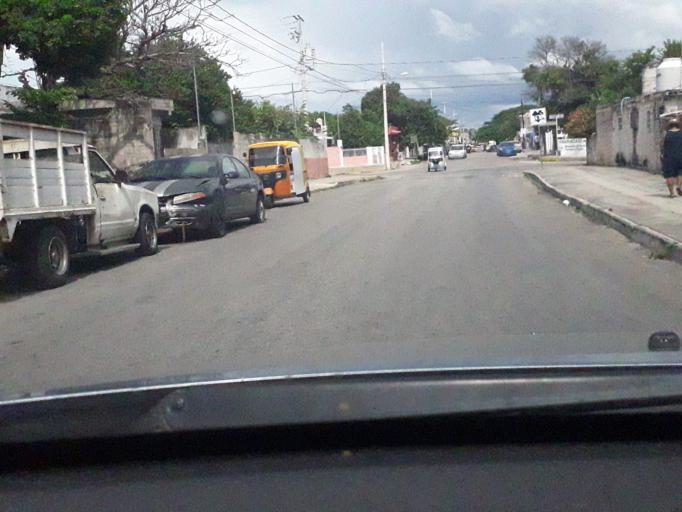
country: MX
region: Yucatan
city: Merida
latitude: 20.9681
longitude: -89.6594
